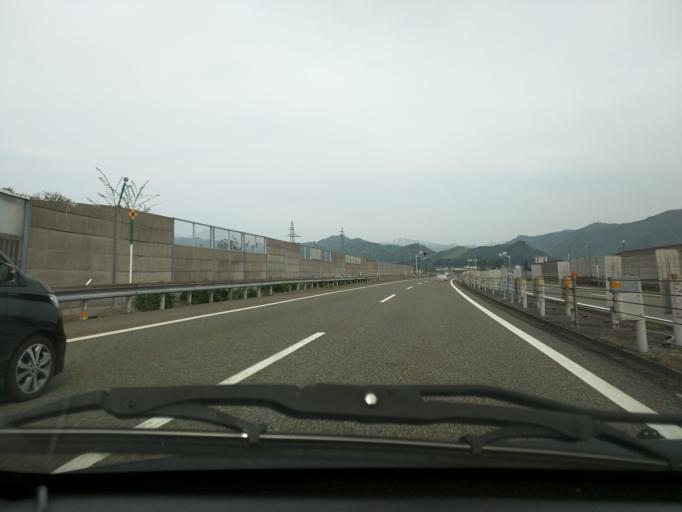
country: JP
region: Niigata
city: Ojiya
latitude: 37.2427
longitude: 138.9627
